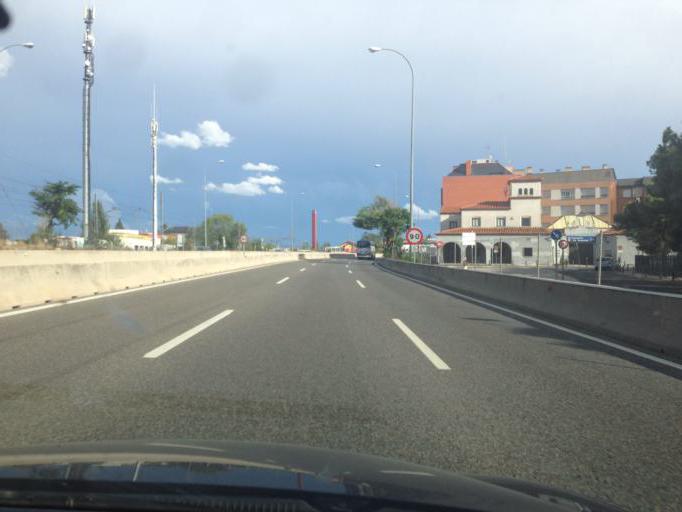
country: ES
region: Madrid
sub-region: Provincia de Madrid
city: Las Rozas de Madrid
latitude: 40.4963
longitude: -3.8699
